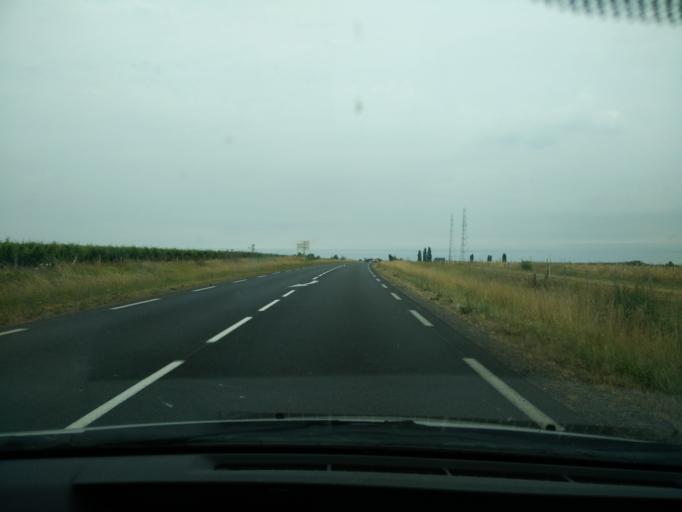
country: FR
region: Pays de la Loire
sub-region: Departement de Maine-et-Loire
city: Doue-la-Fontaine
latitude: 47.1802
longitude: -0.2739
